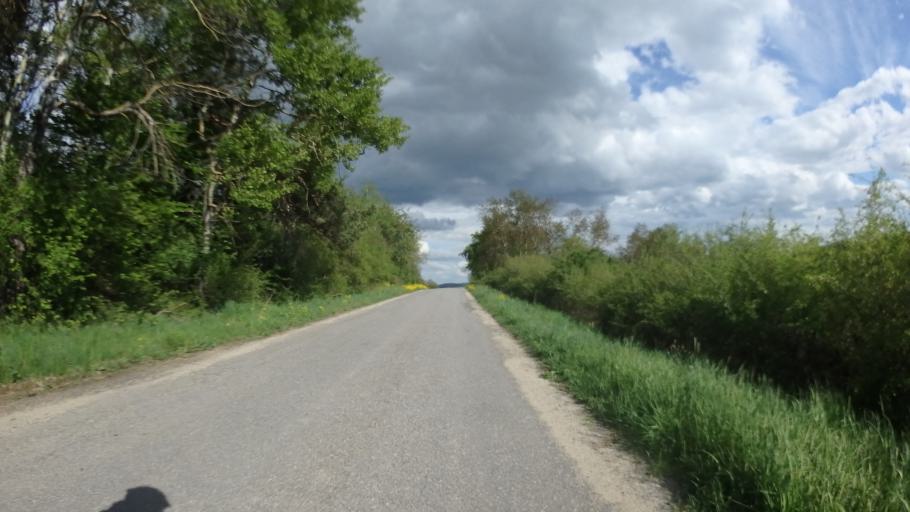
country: CZ
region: Vysocina
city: Merin
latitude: 49.3440
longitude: 15.8864
